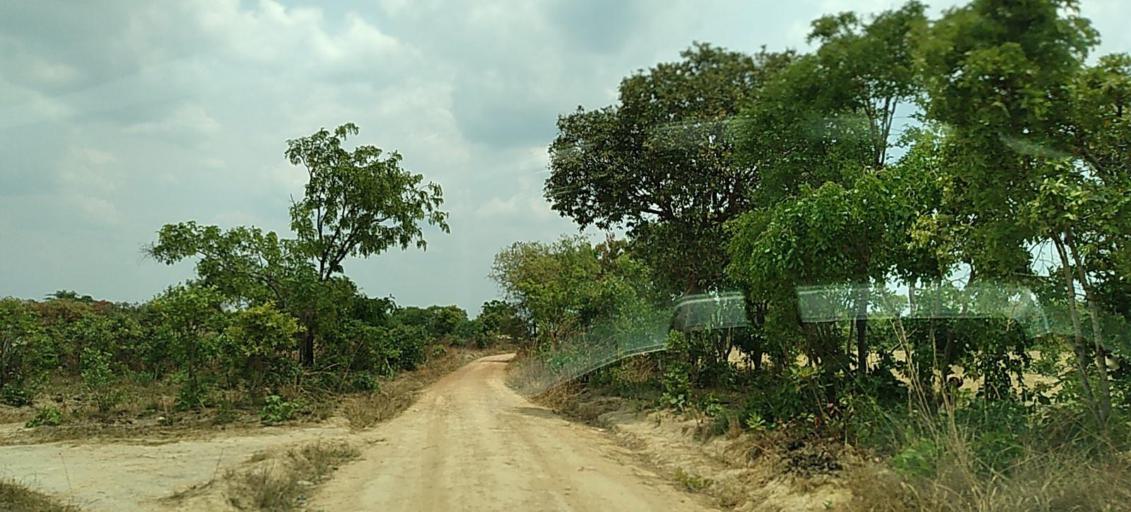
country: ZM
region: Copperbelt
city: Chililabombwe
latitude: -12.3202
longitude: 27.7900
